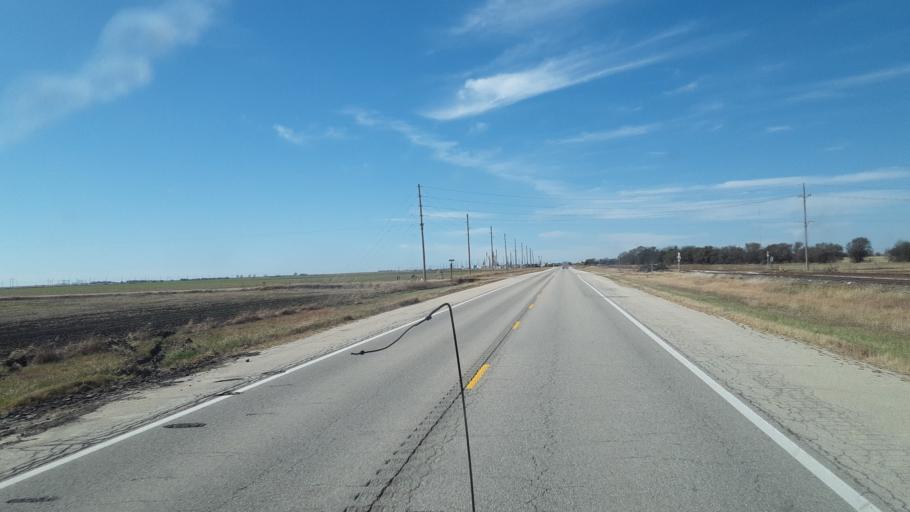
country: US
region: Kansas
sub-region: McPherson County
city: McPherson
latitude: 38.3755
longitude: -97.8123
